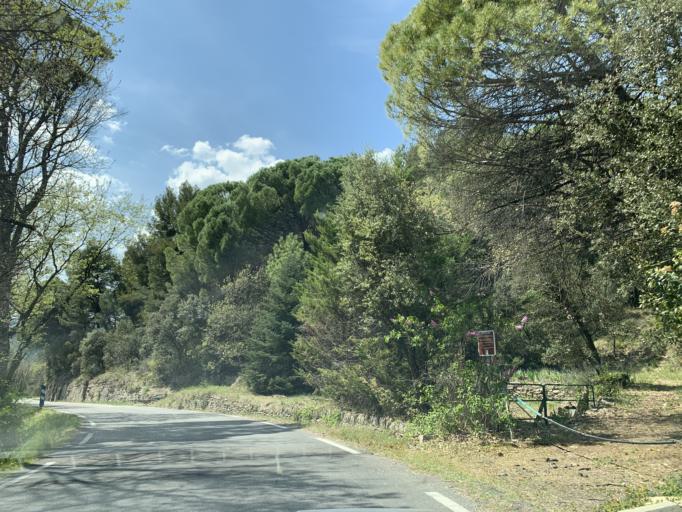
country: FR
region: Provence-Alpes-Cote d'Azur
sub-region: Departement du Vaucluse
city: Goult
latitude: 43.8602
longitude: 5.2378
